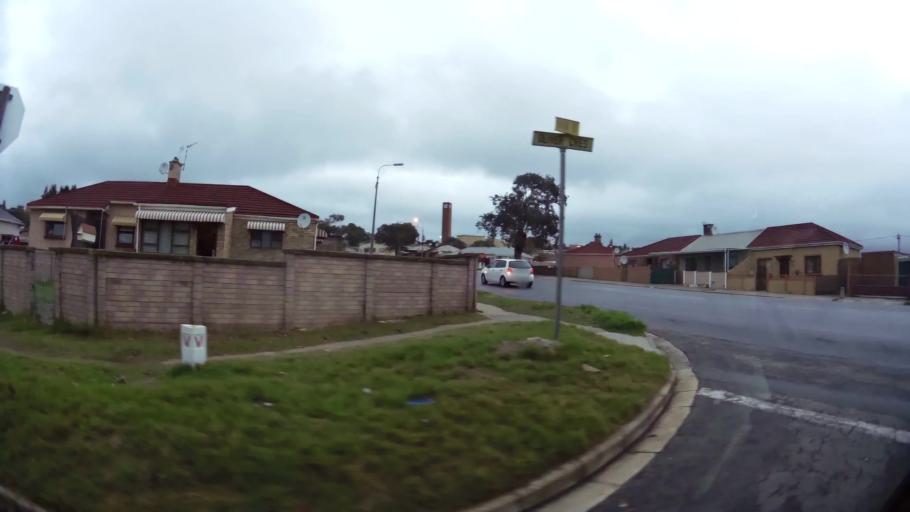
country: ZA
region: Eastern Cape
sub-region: Nelson Mandela Bay Metropolitan Municipality
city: Port Elizabeth
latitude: -33.9408
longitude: 25.5921
